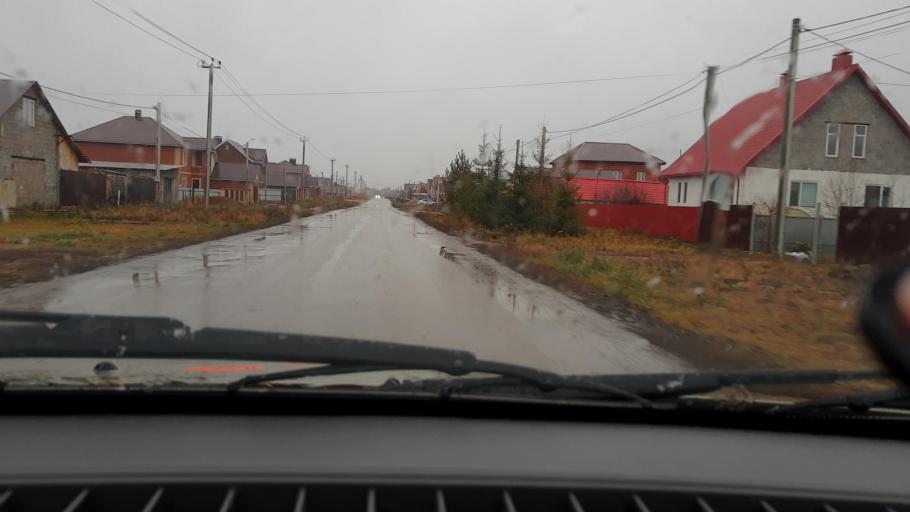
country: RU
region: Bashkortostan
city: Ufa
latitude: 54.6098
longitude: 55.9156
